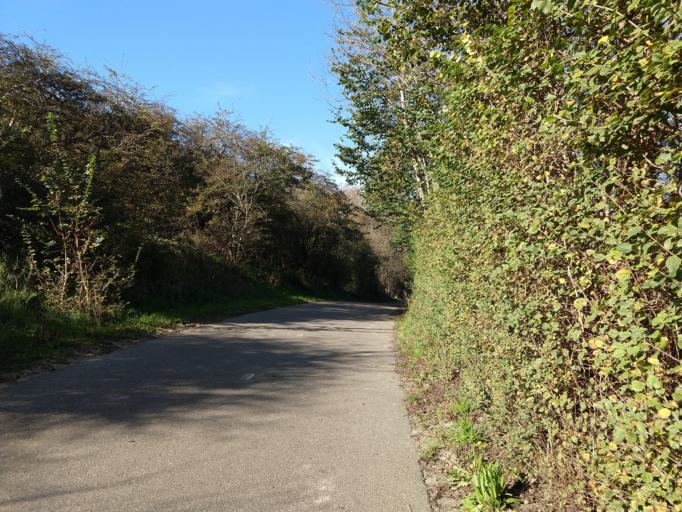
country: NL
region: Zeeland
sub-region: Gemeente Vlissingen
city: Vlissingen
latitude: 51.5113
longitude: 3.4596
